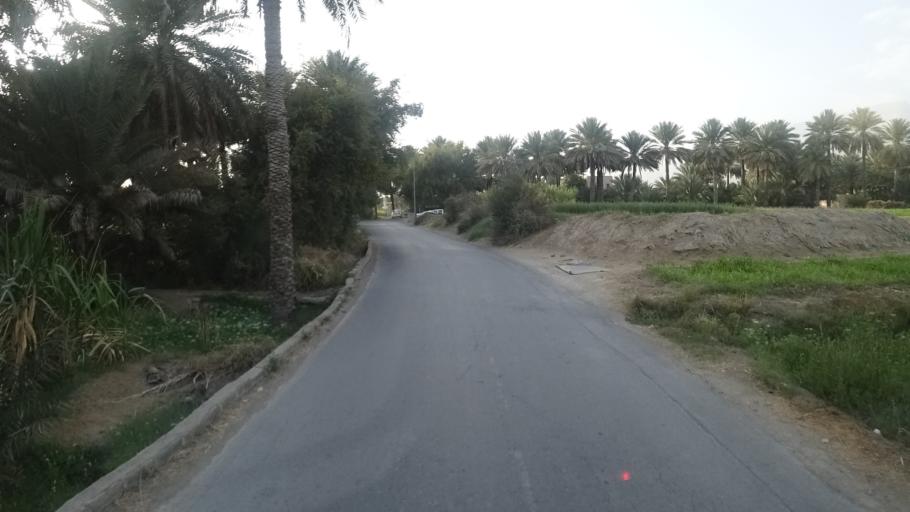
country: OM
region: Muhafazat ad Dakhiliyah
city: Bahla'
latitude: 23.0966
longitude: 57.3093
